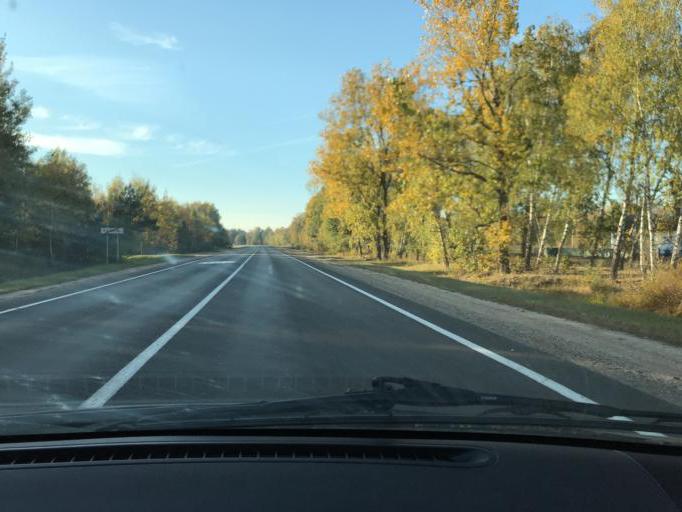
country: BY
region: Brest
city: Horad Kobryn
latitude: 52.2166
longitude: 24.5506
